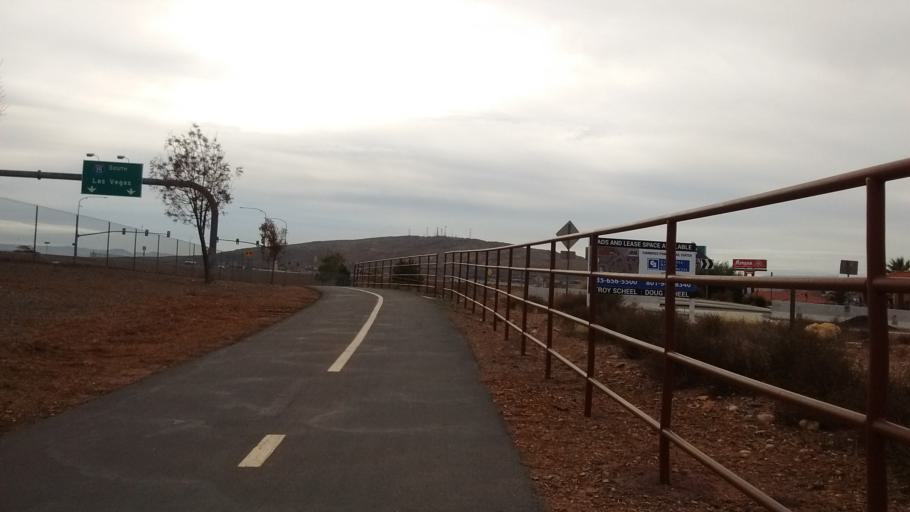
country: US
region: Utah
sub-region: Washington County
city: Saint George
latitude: 37.0855
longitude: -113.5841
